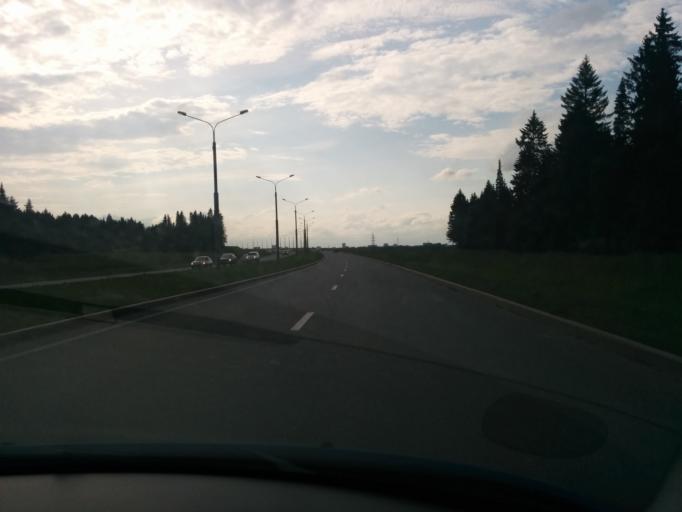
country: RU
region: Perm
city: Perm
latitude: 58.0040
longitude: 56.3704
